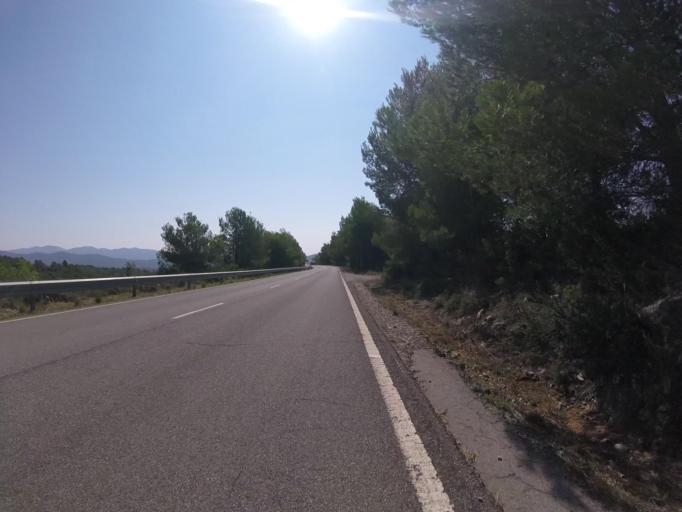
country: ES
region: Valencia
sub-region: Provincia de Castello
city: Benafigos
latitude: 40.2447
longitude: -0.1948
